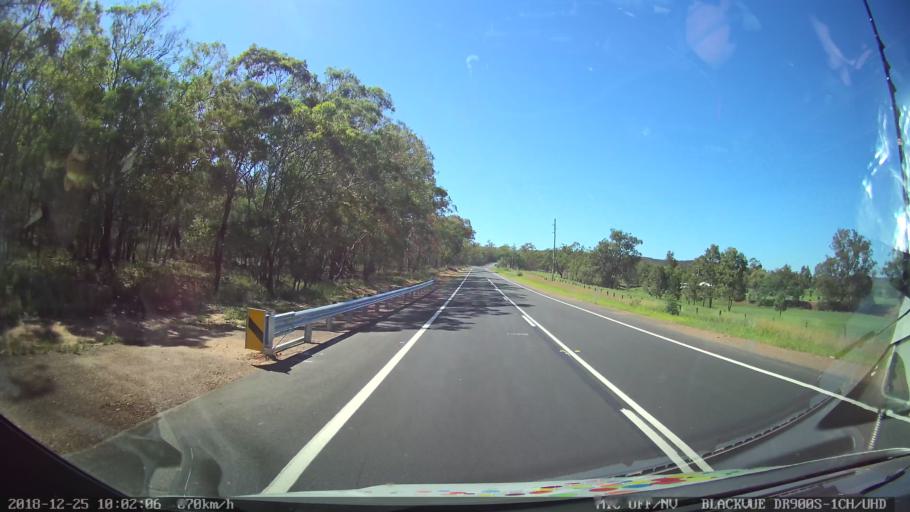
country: AU
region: New South Wales
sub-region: Upper Hunter Shire
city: Merriwa
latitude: -32.2148
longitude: 150.4615
